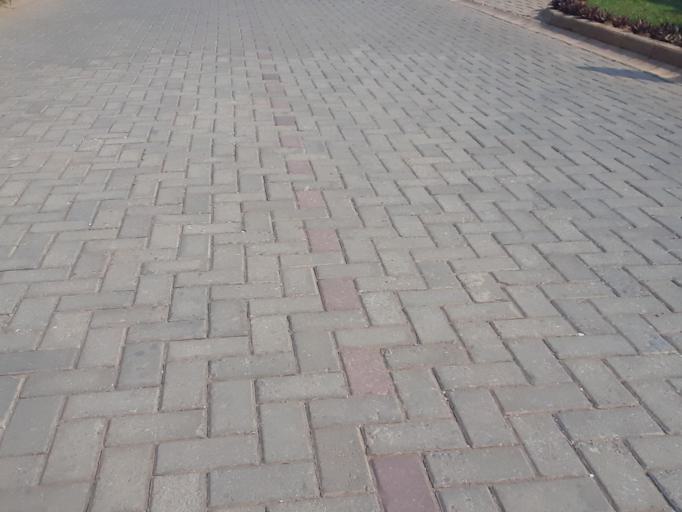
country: ZM
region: Lusaka
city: Lusaka
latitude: -15.3605
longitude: 28.2844
